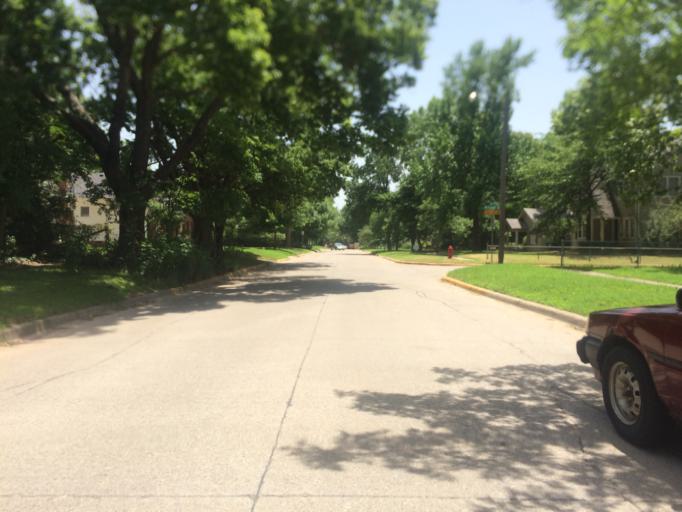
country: US
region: Oklahoma
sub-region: Cleveland County
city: Norman
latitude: 35.2069
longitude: -97.4546
